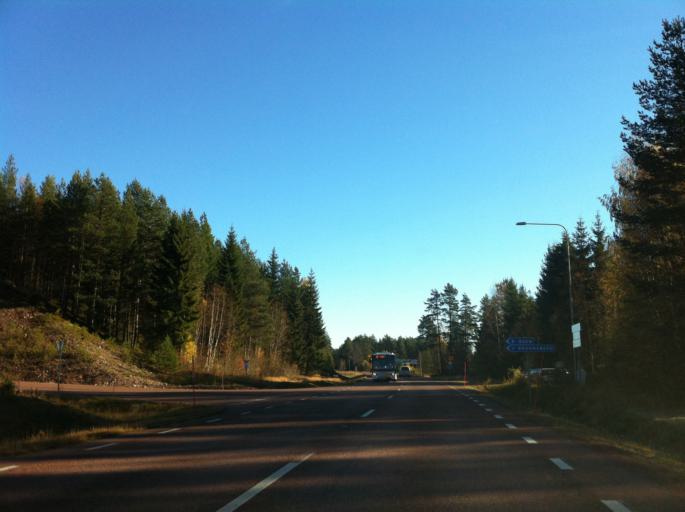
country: SE
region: Dalarna
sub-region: Alvdalens Kommun
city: AElvdalen
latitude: 61.2797
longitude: 13.9543
